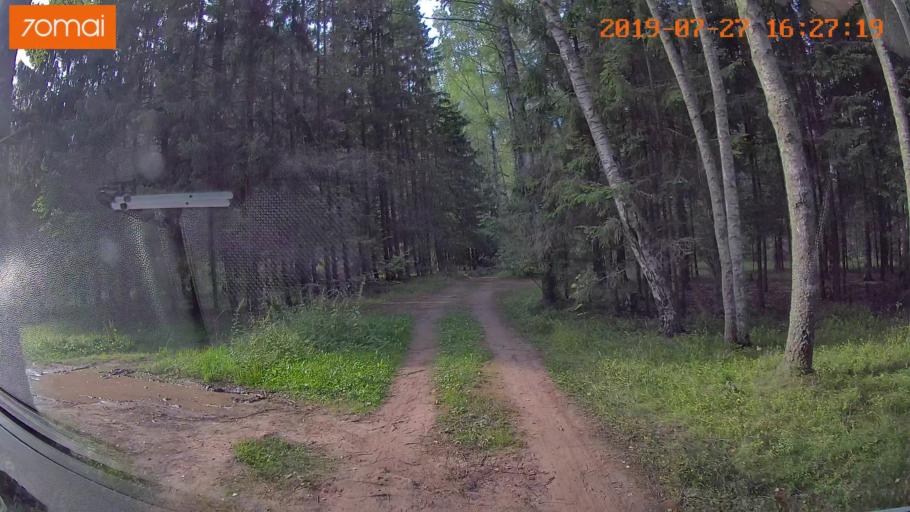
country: RU
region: Ivanovo
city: Novo-Talitsy
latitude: 57.0924
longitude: 40.8533
